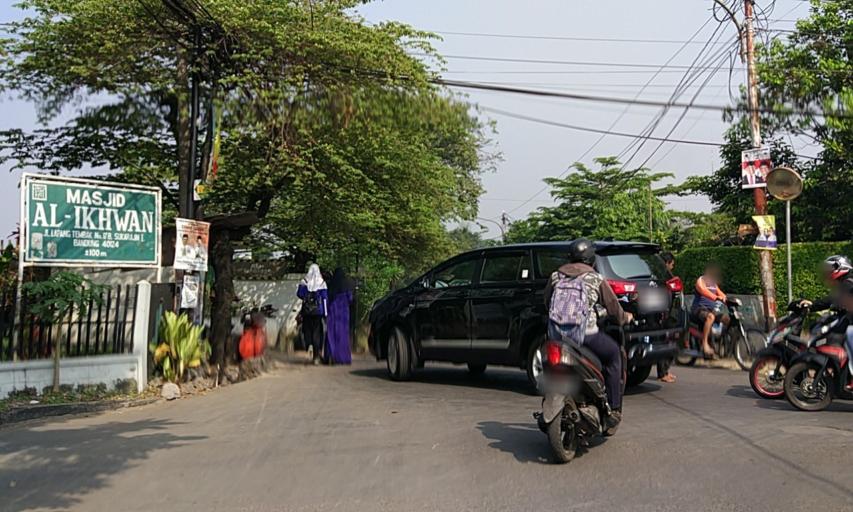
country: ID
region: West Java
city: Bandung
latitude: -6.9011
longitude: 107.6373
